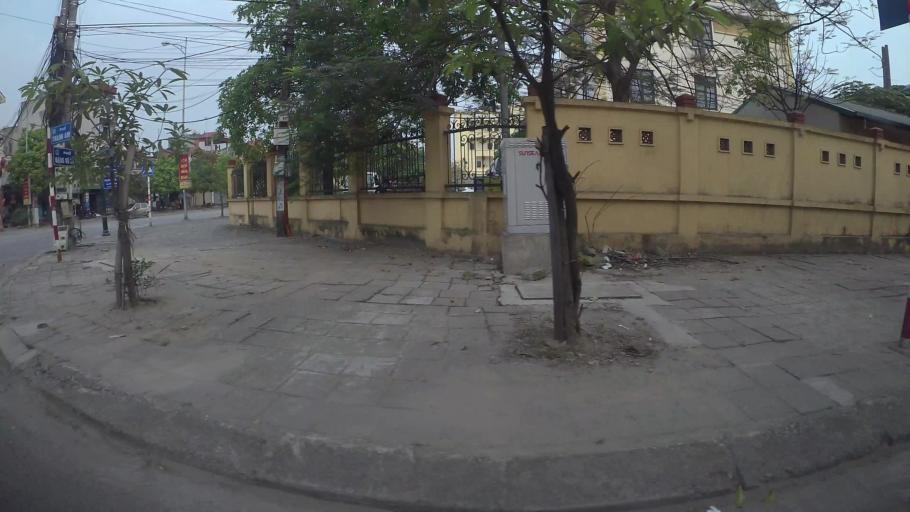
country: VN
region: Ha Noi
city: Trau Quy
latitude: 21.0713
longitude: 105.9001
